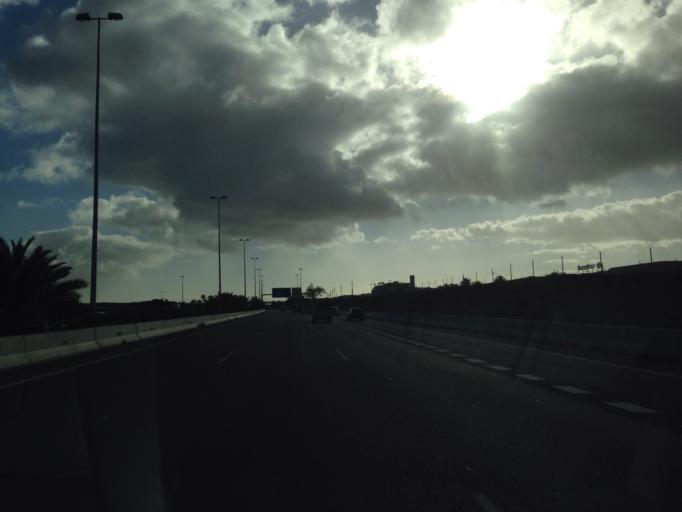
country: ES
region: Canary Islands
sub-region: Provincia de Las Palmas
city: Cruce de Arinaga
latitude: 27.8459
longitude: -15.4360
